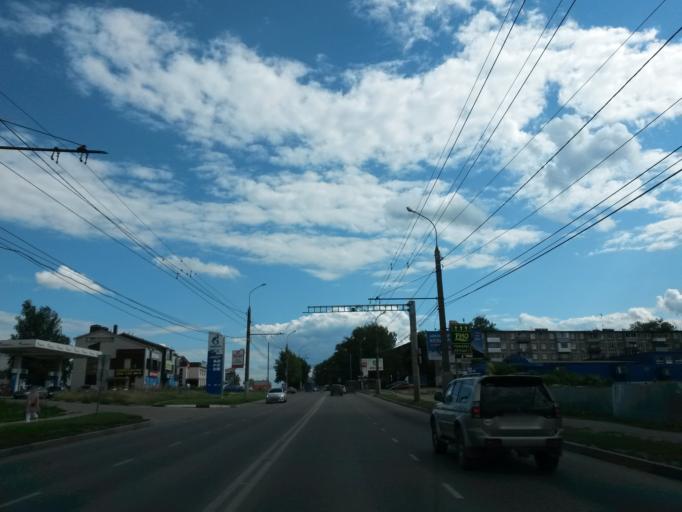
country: RU
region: Ivanovo
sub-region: Gorod Ivanovo
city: Ivanovo
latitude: 56.9758
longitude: 41.0068
